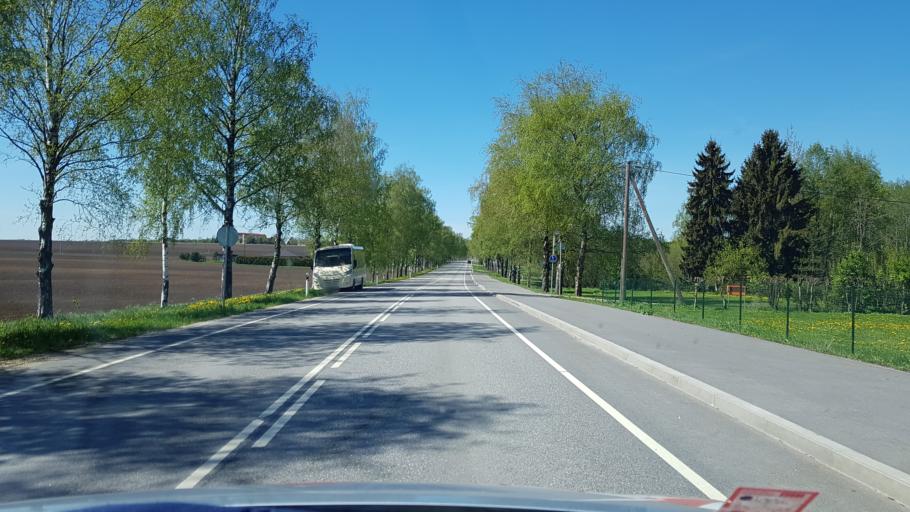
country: EE
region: Tartu
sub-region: Noo vald
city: Noo
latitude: 58.3883
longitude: 26.5750
